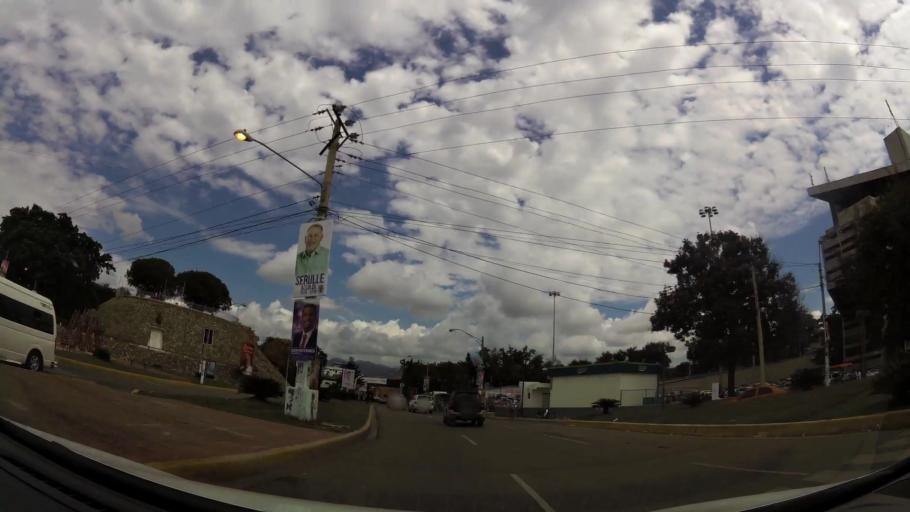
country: DO
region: Santiago
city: Santiago de los Caballeros
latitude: 19.4563
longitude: -70.7074
